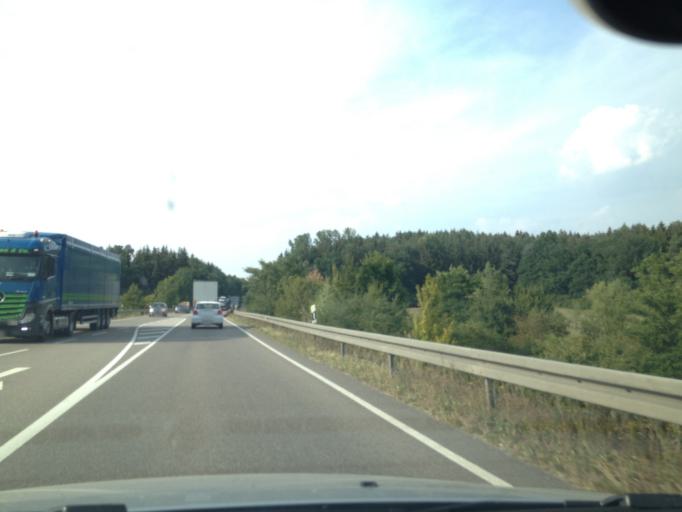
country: DE
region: Bavaria
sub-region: Swabia
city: Monheim
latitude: 48.8269
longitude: 10.8282
